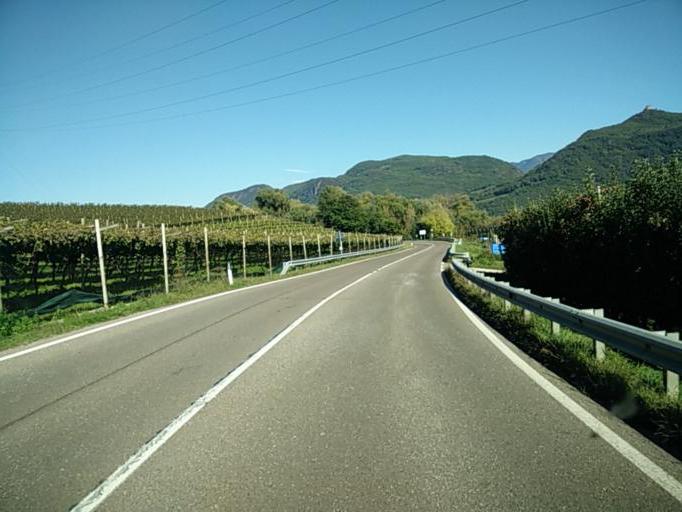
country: IT
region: Trentino-Alto Adige
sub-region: Bolzano
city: Termeno
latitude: 46.3693
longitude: 11.2514
